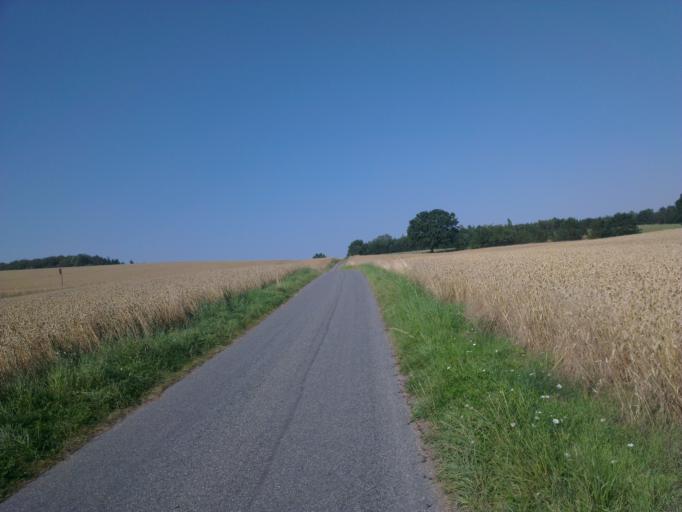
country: DK
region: Capital Region
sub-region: Frederikssund Kommune
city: Skibby
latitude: 55.7612
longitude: 11.9414
